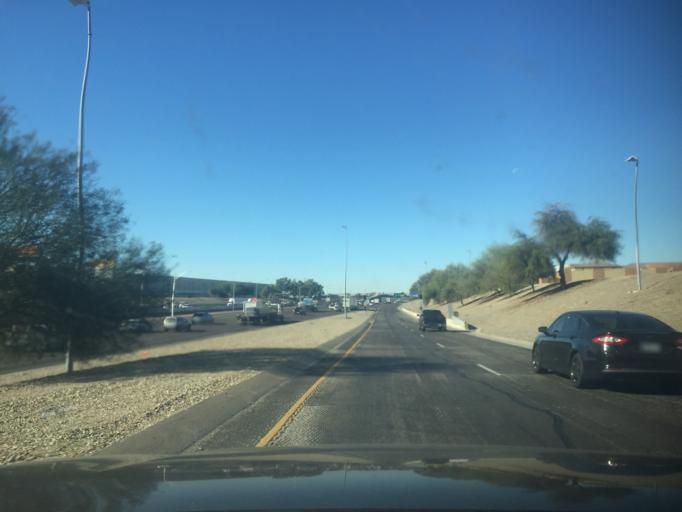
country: US
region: Arizona
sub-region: Maricopa County
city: Tolleson
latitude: 33.4631
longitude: -112.2226
